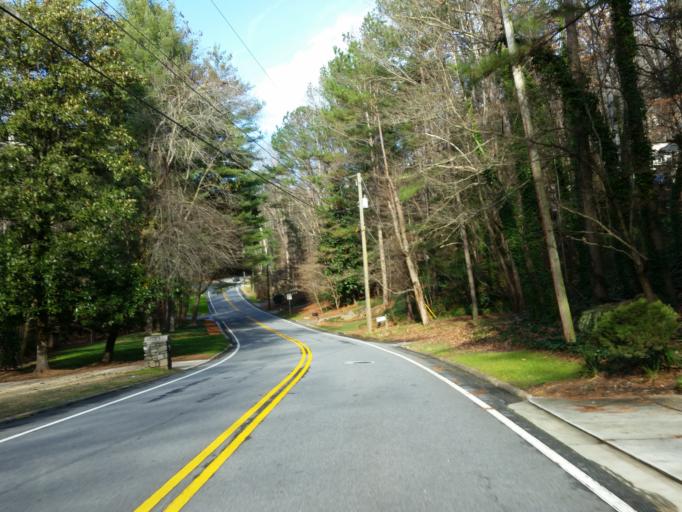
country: US
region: Georgia
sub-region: Fulton County
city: Sandy Springs
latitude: 33.9471
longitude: -84.3943
